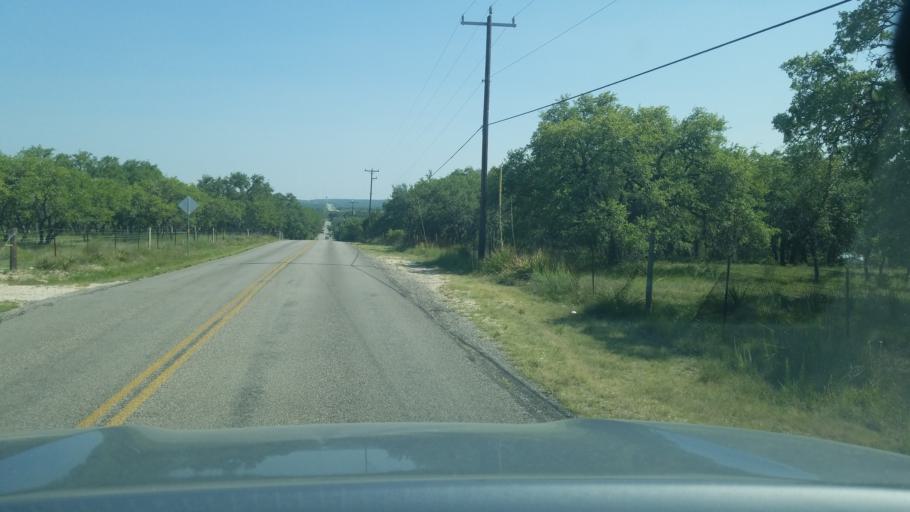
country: US
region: Texas
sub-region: Bexar County
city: Timberwood Park
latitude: 29.7556
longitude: -98.5128
